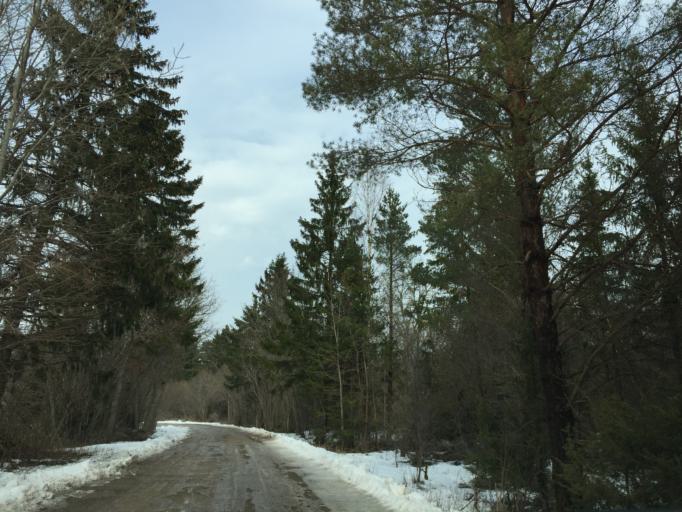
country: EE
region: Saare
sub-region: Kuressaare linn
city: Kuressaare
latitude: 58.4244
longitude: 22.1519
